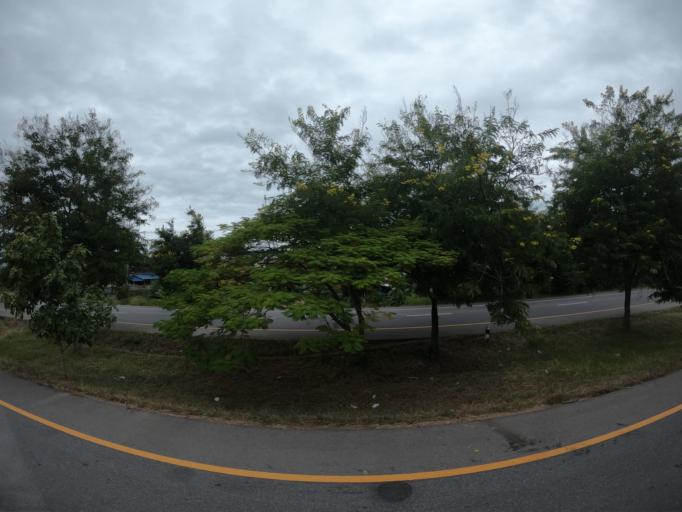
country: TH
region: Maha Sarakham
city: Maha Sarakham
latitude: 16.1514
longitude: 103.3808
